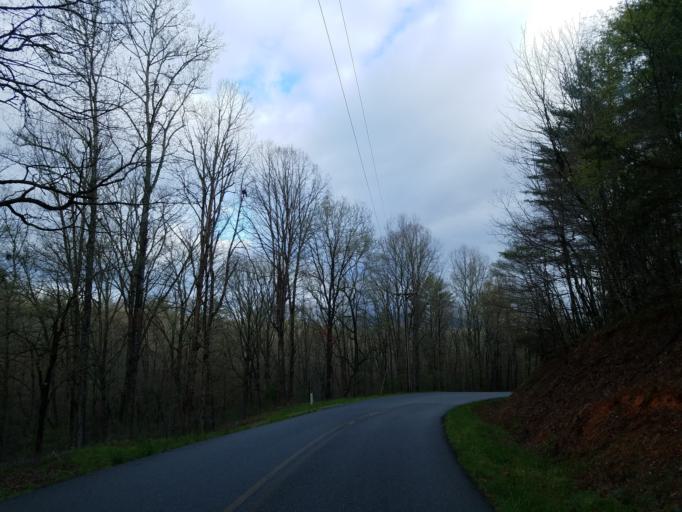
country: US
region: Georgia
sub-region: Fannin County
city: Blue Ridge
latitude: 34.7700
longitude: -84.2319
